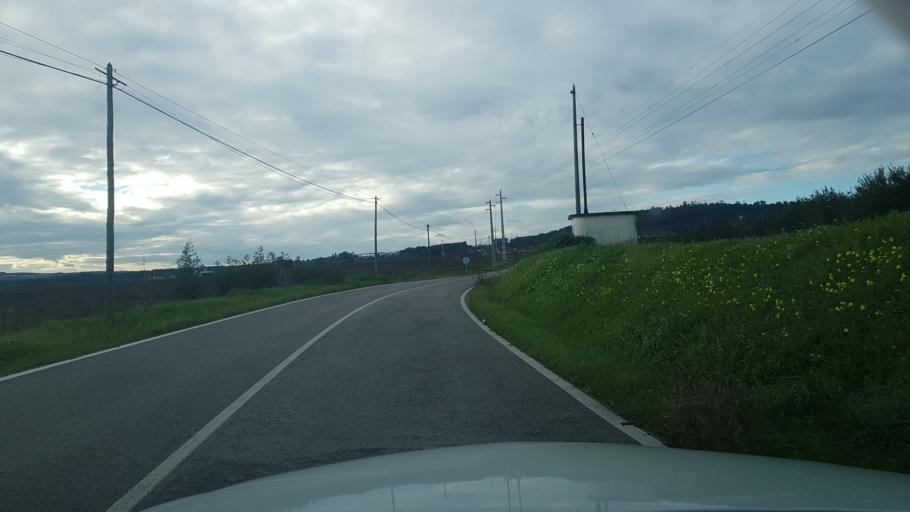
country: PT
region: Santarem
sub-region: Abrantes
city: Tramagal
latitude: 39.4839
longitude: -8.2576
